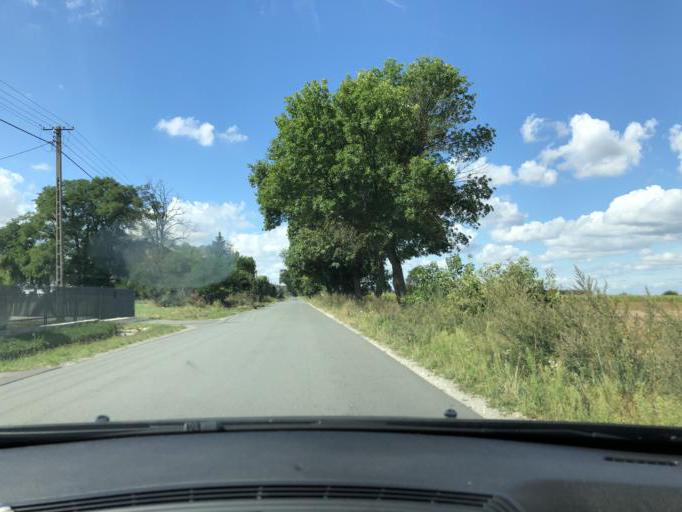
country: PL
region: Lodz Voivodeship
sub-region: Powiat wieruszowski
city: Czastary
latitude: 51.2415
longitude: 18.3538
